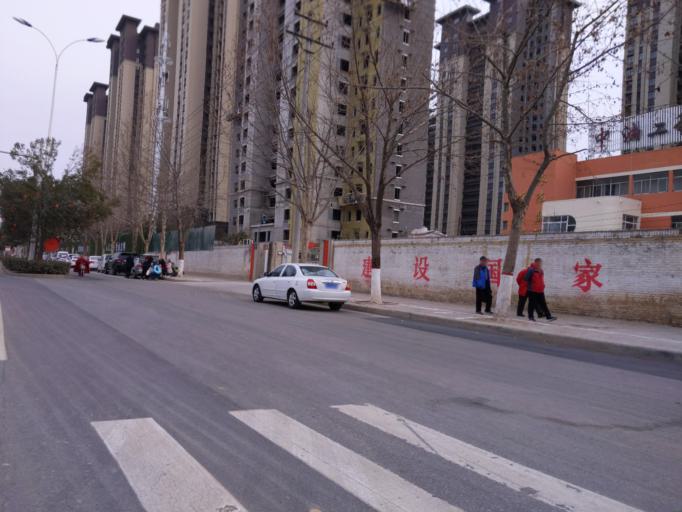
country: CN
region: Henan Sheng
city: Zhongyuanlu
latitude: 35.7578
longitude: 115.0736
